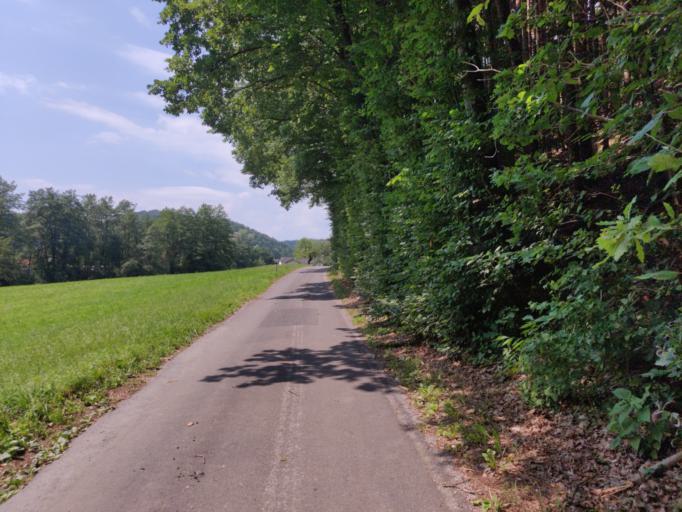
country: AT
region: Styria
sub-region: Politischer Bezirk Graz-Umgebung
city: Gratwein
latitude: 47.1080
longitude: 15.2920
